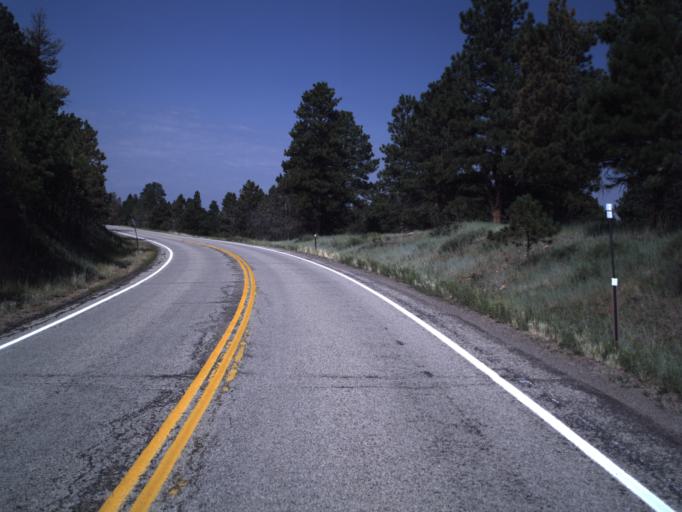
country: US
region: Utah
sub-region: Daggett County
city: Manila
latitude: 40.8704
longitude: -109.5061
